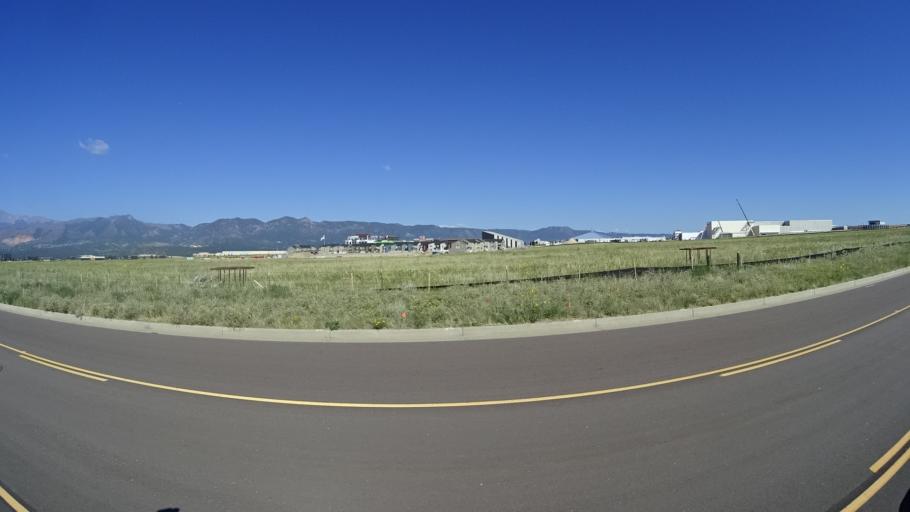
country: US
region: Colorado
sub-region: El Paso County
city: Gleneagle
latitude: 38.9856
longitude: -104.7878
